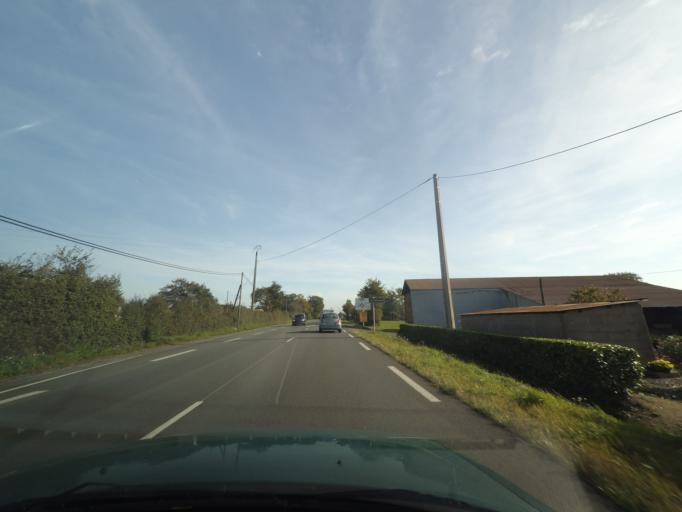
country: FR
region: Pays de la Loire
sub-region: Departement de Maine-et-Loire
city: Torfou
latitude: 47.0304
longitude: -1.0946
